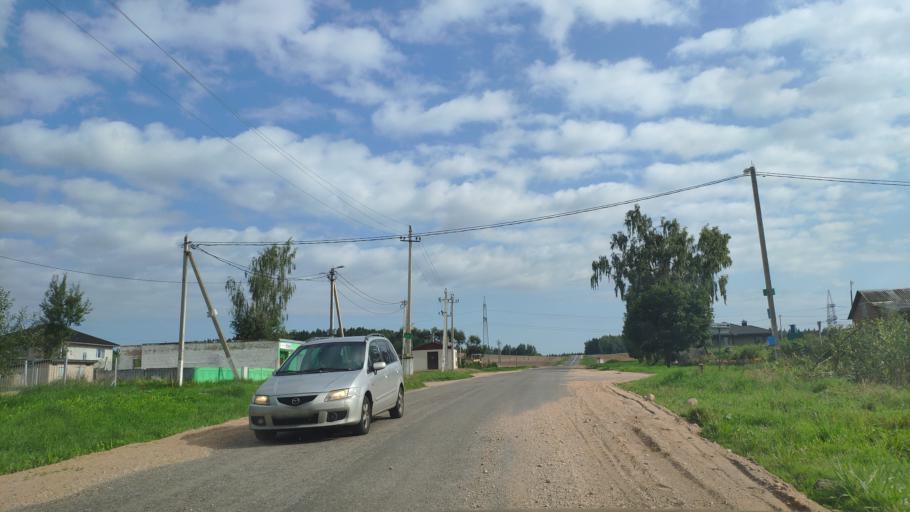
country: BY
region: Minsk
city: Khatsyezhyna
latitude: 53.8676
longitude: 27.3174
